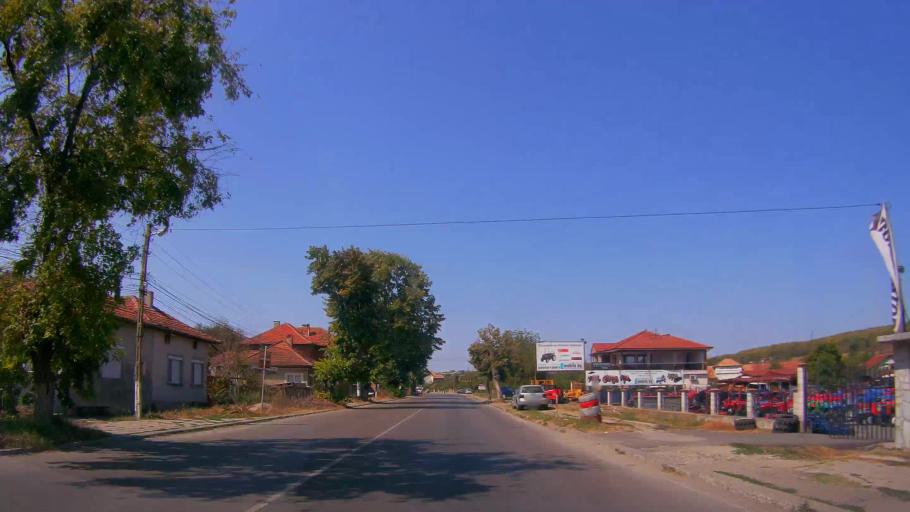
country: BG
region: Razgrad
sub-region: Obshtina Tsar Kaloyan
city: Tsar Kaloyan
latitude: 43.6099
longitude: 26.2346
